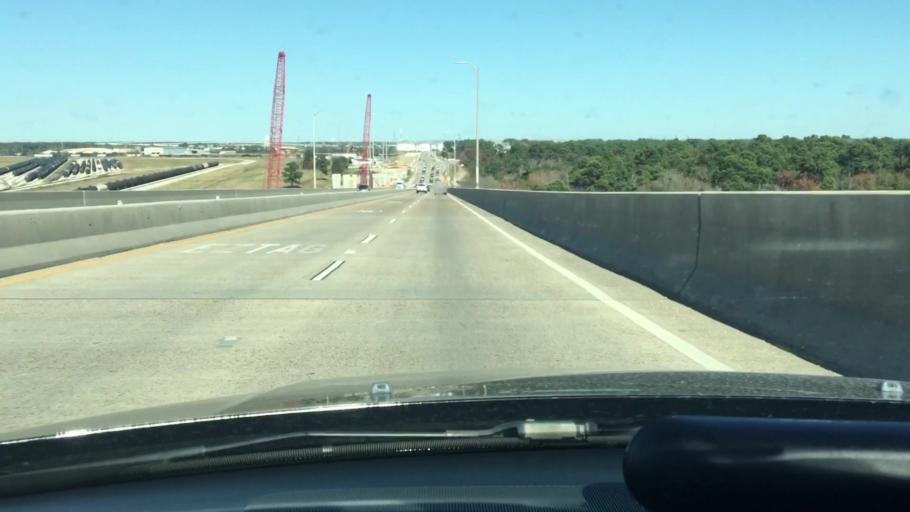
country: US
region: Texas
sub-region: Harris County
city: Deer Park
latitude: 29.7426
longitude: -95.1456
